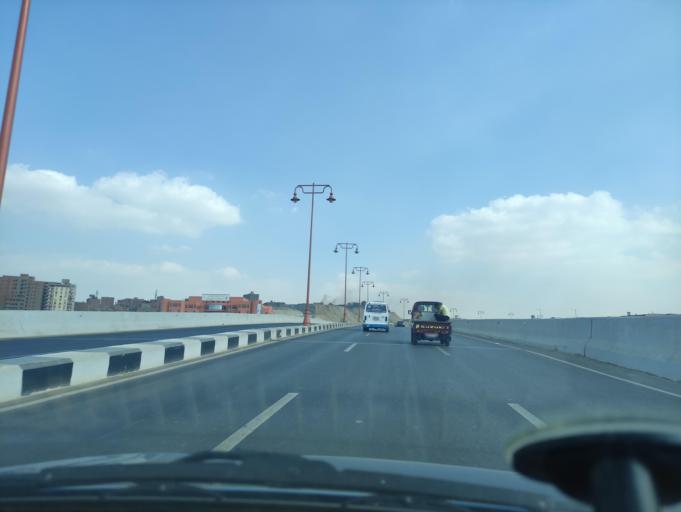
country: EG
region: Muhafazat al Qahirah
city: Cairo
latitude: 30.0507
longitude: 31.2853
